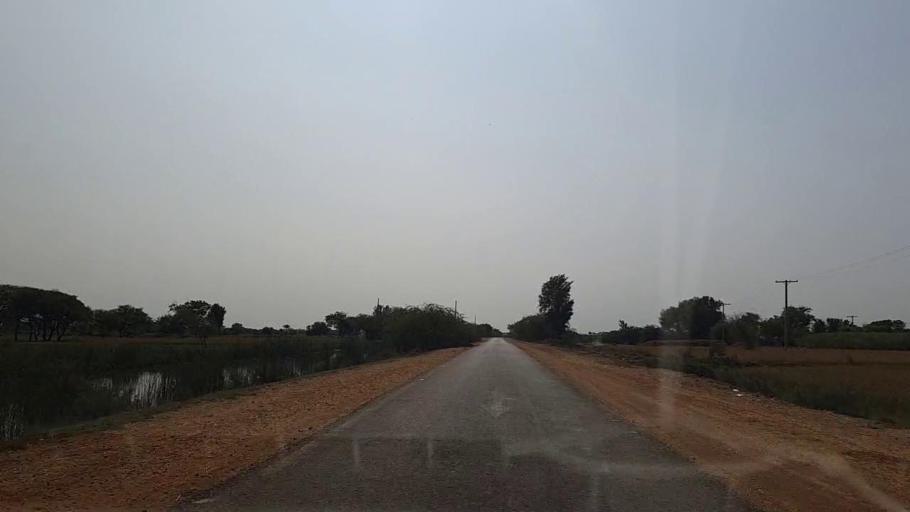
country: PK
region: Sindh
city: Chuhar Jamali
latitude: 24.3174
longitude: 67.9403
